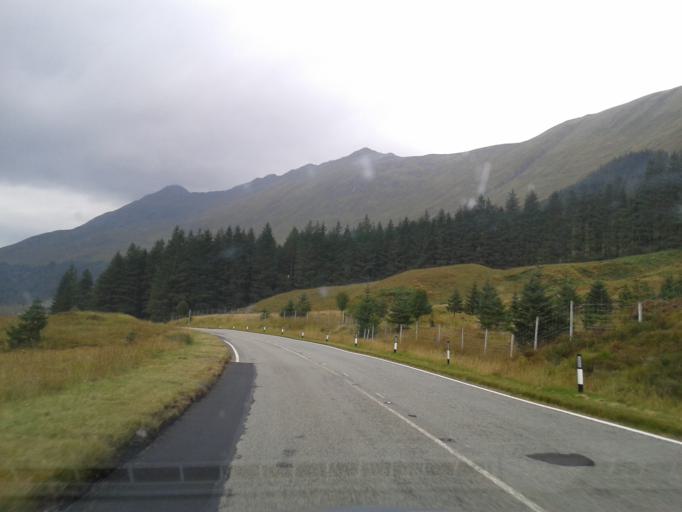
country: GB
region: Scotland
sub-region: Highland
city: Fort William
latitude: 57.1656
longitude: -5.2772
